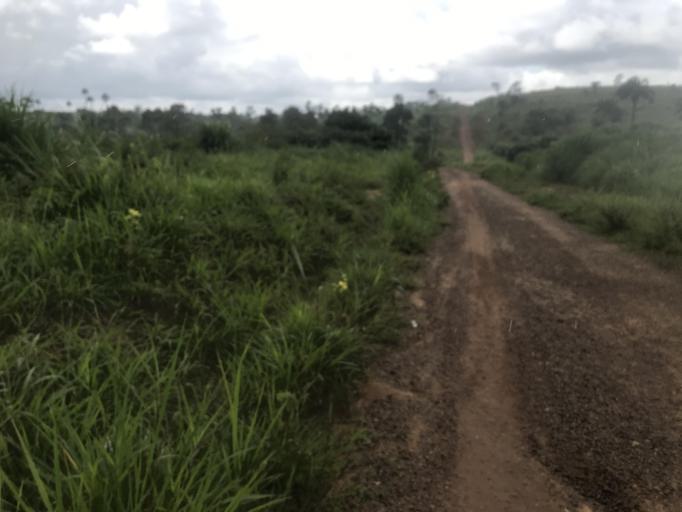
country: GN
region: Nzerekore
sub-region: Prefecture de Guekedou
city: Gueckedou
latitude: 8.4777
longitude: -10.2937
